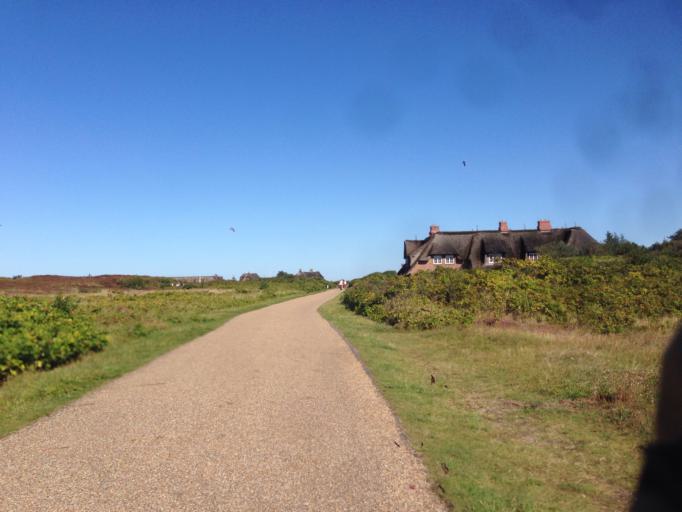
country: DE
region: Schleswig-Holstein
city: Tinnum
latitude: 54.9532
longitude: 8.3374
